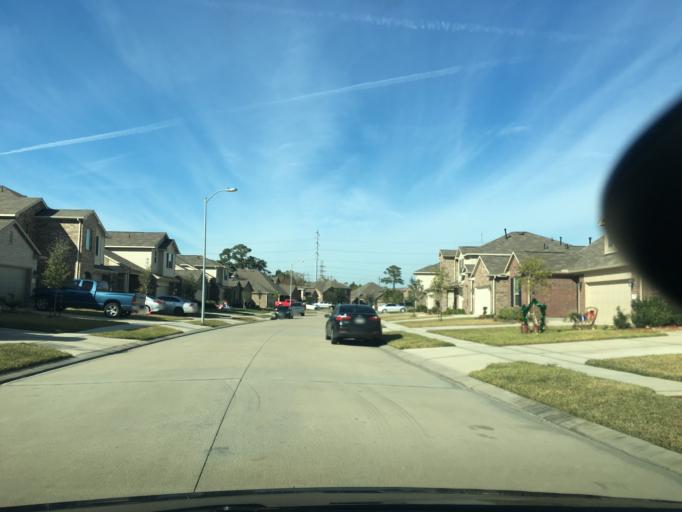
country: US
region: Texas
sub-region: Harris County
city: Cloverleaf
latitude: 29.8141
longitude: -95.1610
